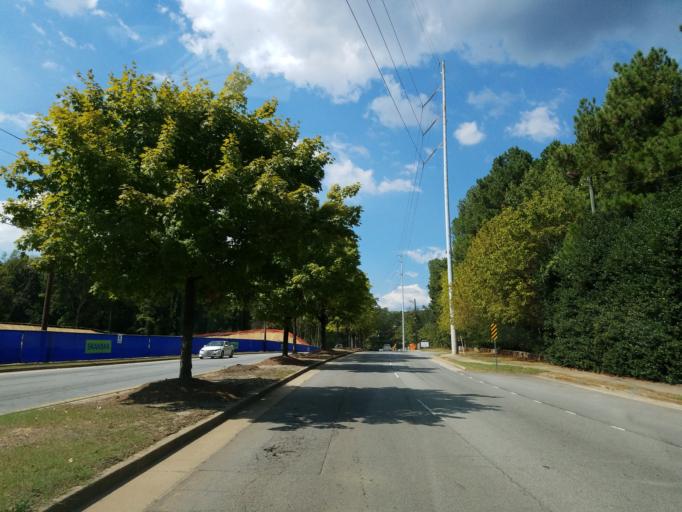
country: US
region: Georgia
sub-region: Fulton County
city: Sandy Springs
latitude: 33.9343
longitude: -84.3627
